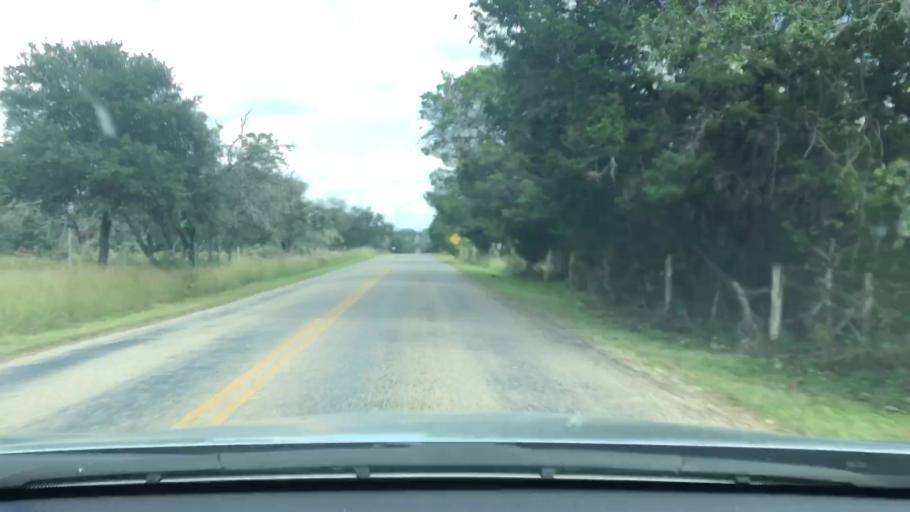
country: US
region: Texas
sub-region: Bexar County
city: Fair Oaks Ranch
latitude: 29.7856
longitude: -98.6546
